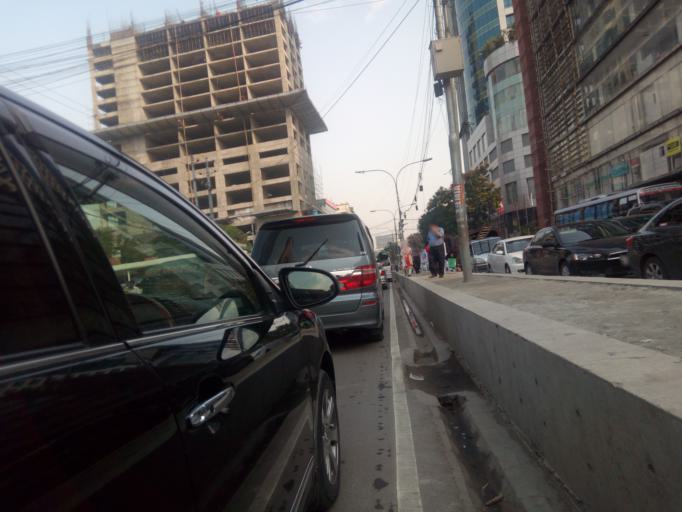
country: BD
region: Dhaka
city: Paltan
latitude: 23.7941
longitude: 90.4146
